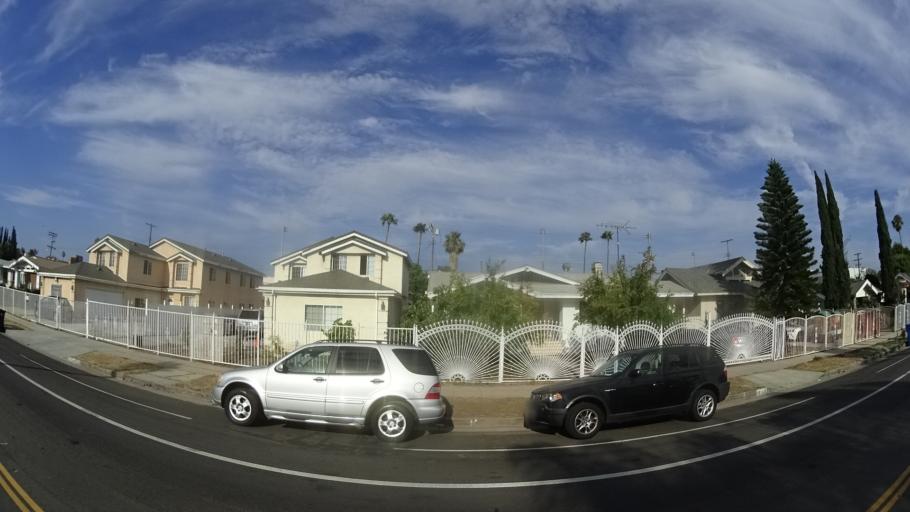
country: US
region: California
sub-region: Los Angeles County
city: Silver Lake
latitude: 34.0853
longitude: -118.2959
